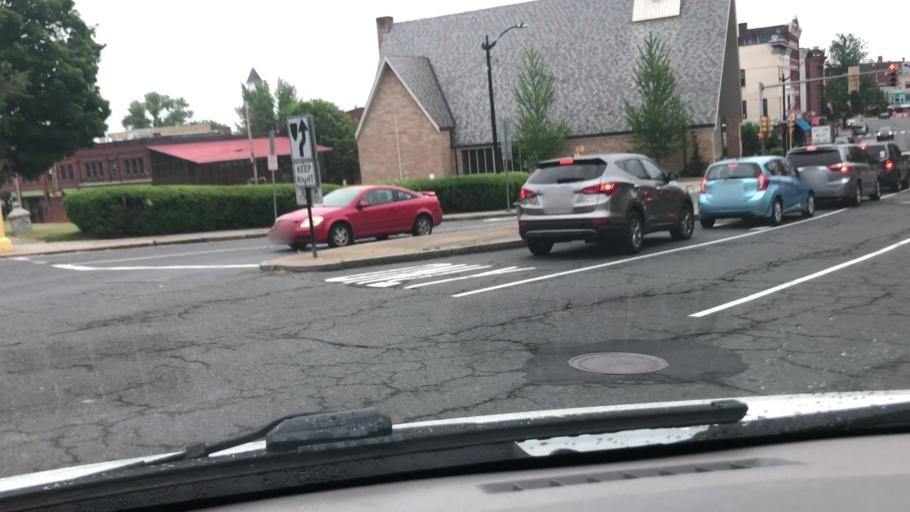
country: US
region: Massachusetts
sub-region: Hampshire County
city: Northampton
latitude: 42.3177
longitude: -72.6348
